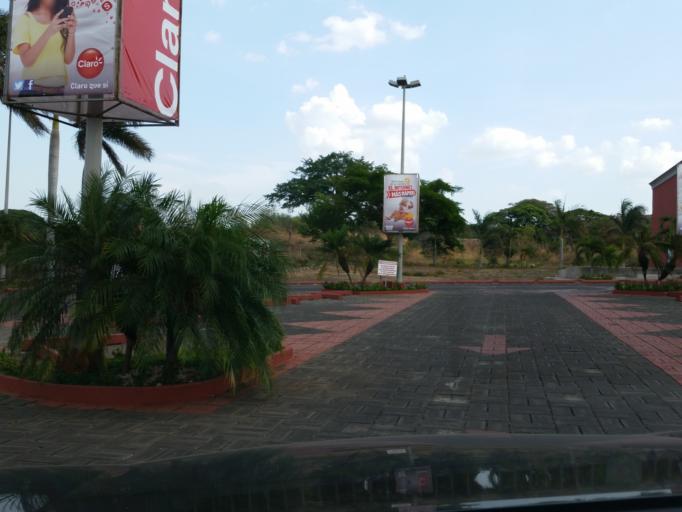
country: NI
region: Managua
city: Managua
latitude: 12.1018
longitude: -86.2451
